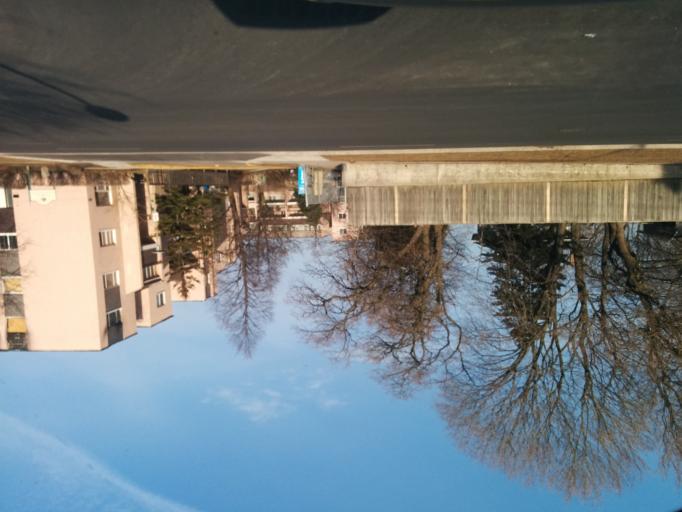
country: CA
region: Ontario
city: Etobicoke
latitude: 43.6017
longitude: -79.5955
